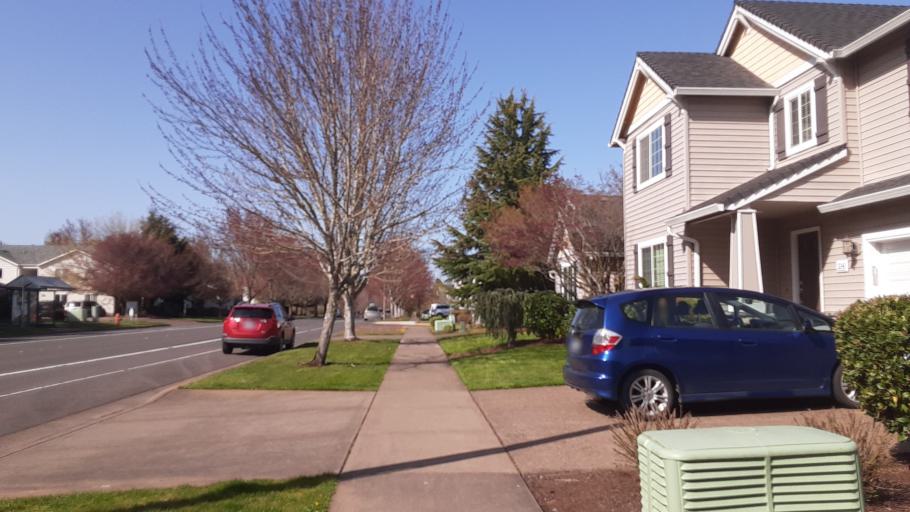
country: US
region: Oregon
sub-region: Benton County
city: Corvallis
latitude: 44.5328
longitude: -123.2564
